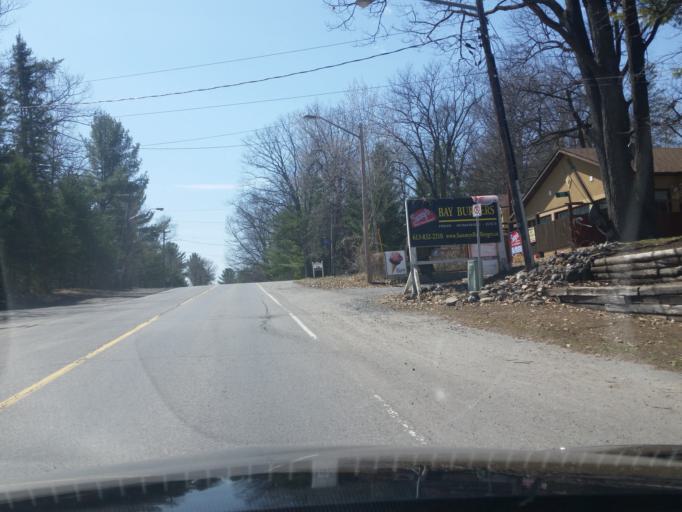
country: CA
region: Ontario
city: Arnprior
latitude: 45.4859
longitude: -76.0739
